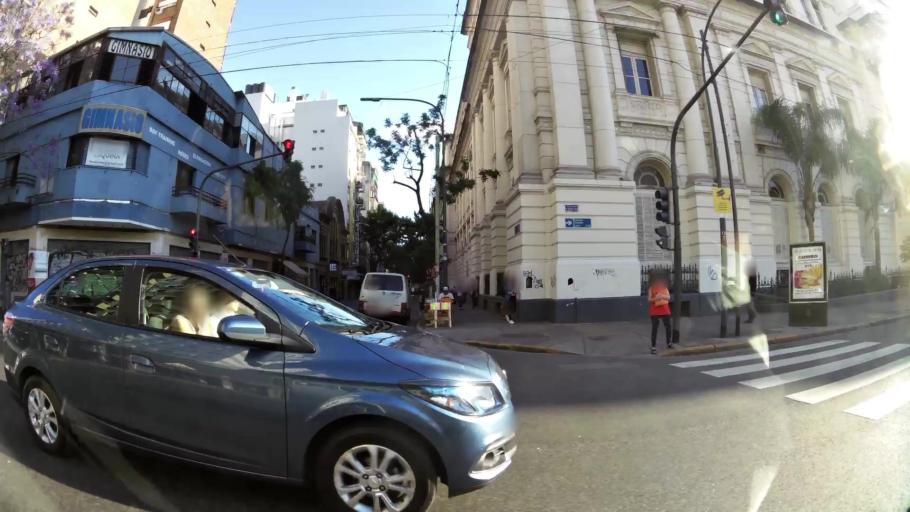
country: AR
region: Buenos Aires F.D.
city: Retiro
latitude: -34.5996
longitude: -58.3973
